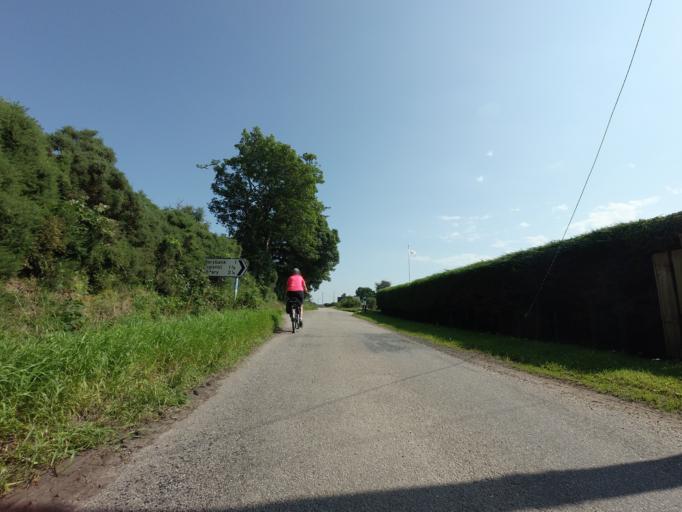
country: GB
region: Scotland
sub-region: Highland
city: Tain
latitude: 57.7600
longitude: -4.1190
